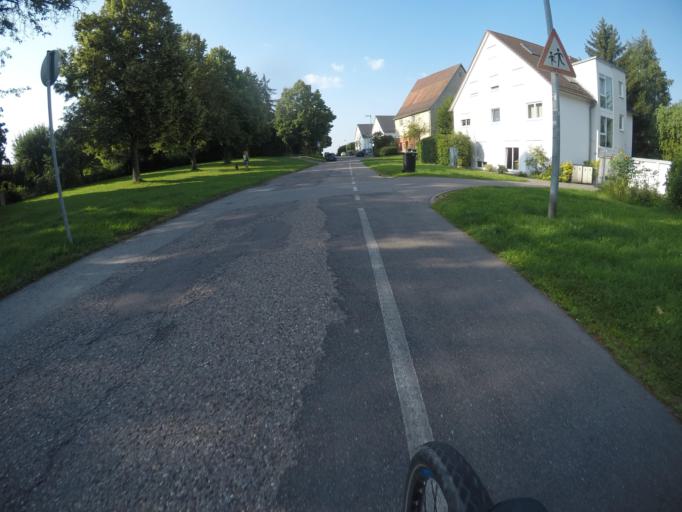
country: DE
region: Baden-Wuerttemberg
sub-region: Regierungsbezirk Stuttgart
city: Herrenberg
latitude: 48.5909
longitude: 8.8701
